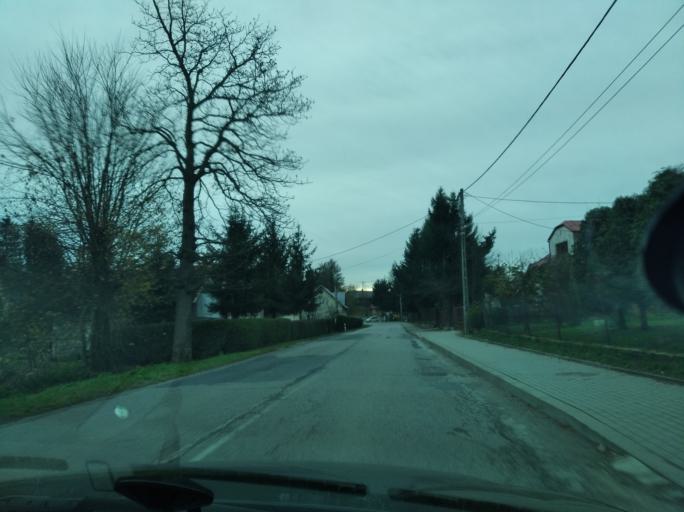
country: PL
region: Subcarpathian Voivodeship
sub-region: Powiat lancucki
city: Krzemienica
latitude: 50.0762
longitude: 22.1891
